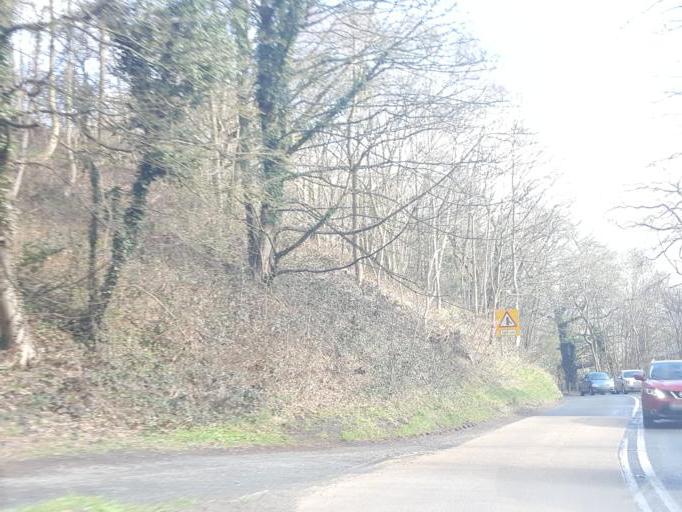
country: GB
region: England
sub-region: Worcestershire
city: Great Malvern
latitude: 52.0626
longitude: -2.3398
